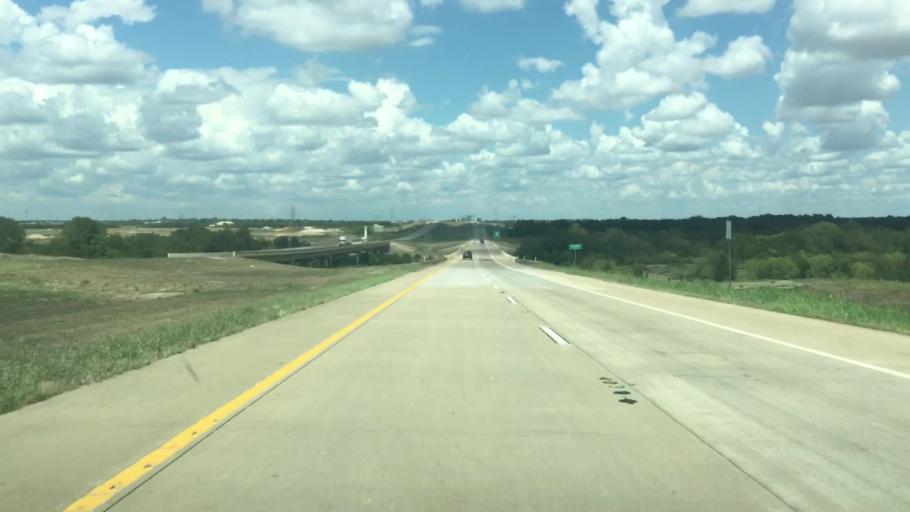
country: US
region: Texas
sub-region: Williamson County
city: Georgetown
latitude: 30.6520
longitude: -97.6350
